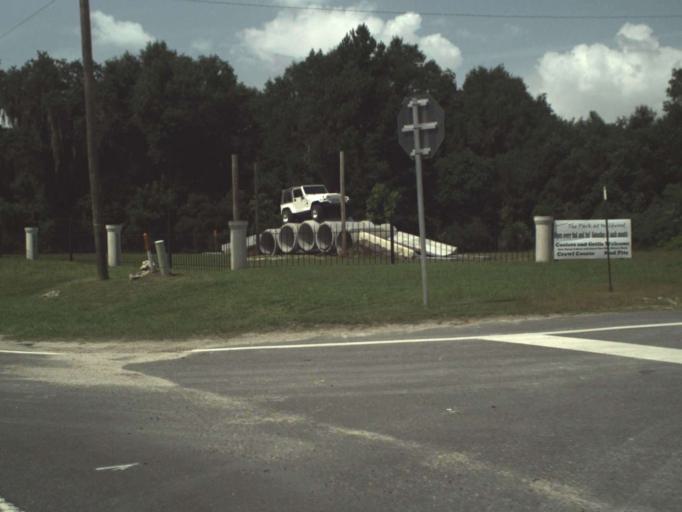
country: US
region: Florida
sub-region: Sumter County
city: Wildwood
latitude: 28.8161
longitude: -82.0456
